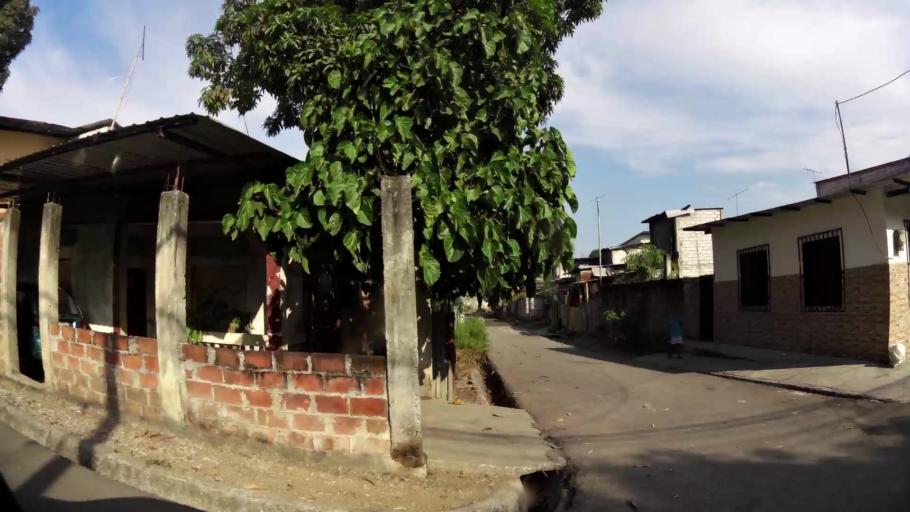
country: EC
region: Guayas
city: Eloy Alfaro
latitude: -2.0751
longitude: -79.9329
